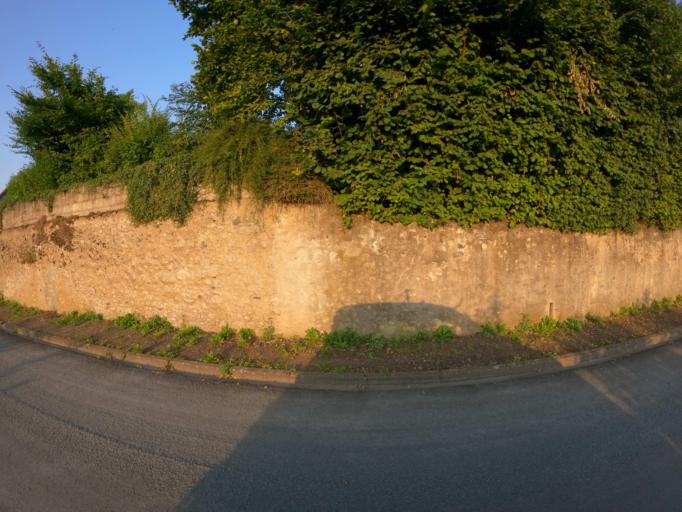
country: FR
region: Pays de la Loire
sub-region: Departement de la Sarthe
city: Parce-sur-Sarthe
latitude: 47.9026
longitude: -0.2222
